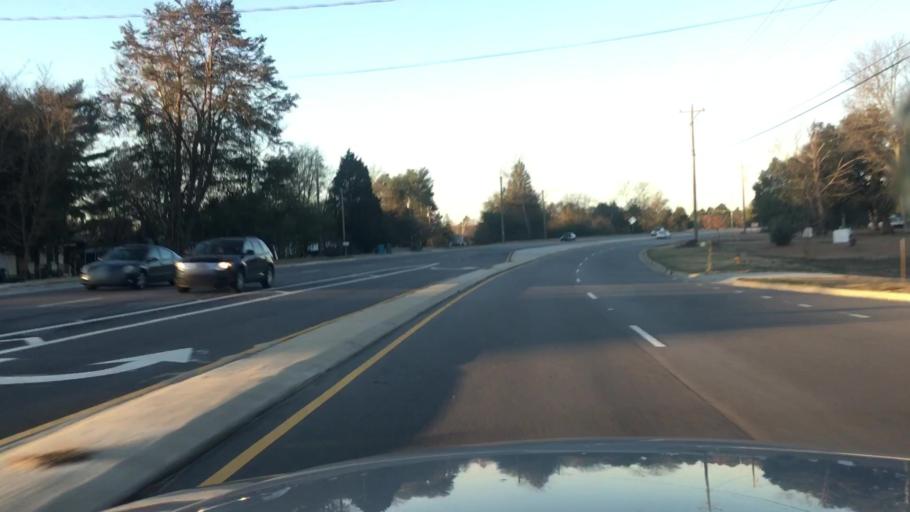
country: US
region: North Carolina
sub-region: Cumberland County
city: Hope Mills
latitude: 34.9993
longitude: -78.9305
